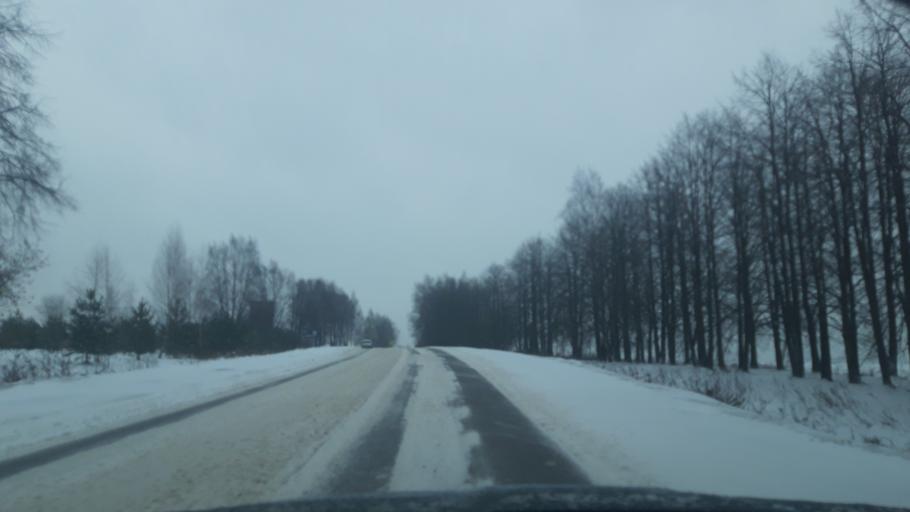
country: RU
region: Moskovskaya
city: Yakhroma
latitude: 56.2984
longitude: 37.4600
